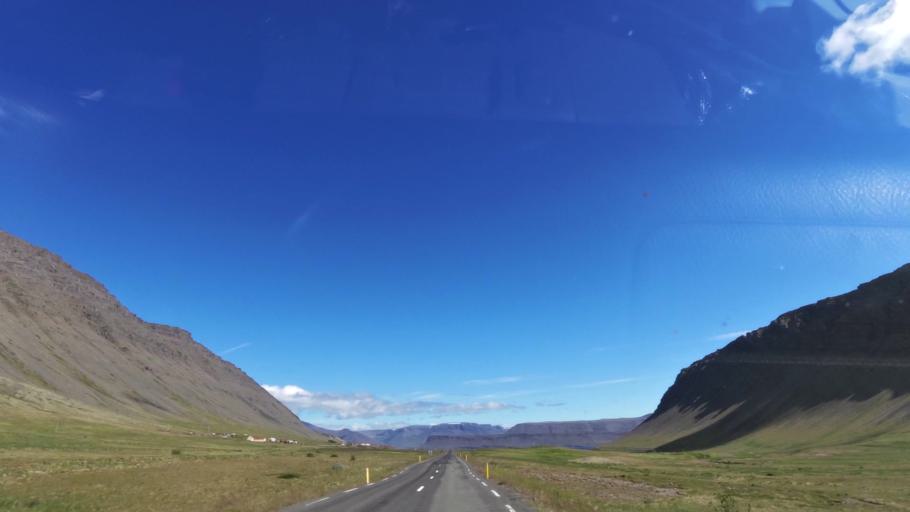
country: IS
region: Westfjords
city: Isafjoerdur
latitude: 65.6676
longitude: -23.6327
